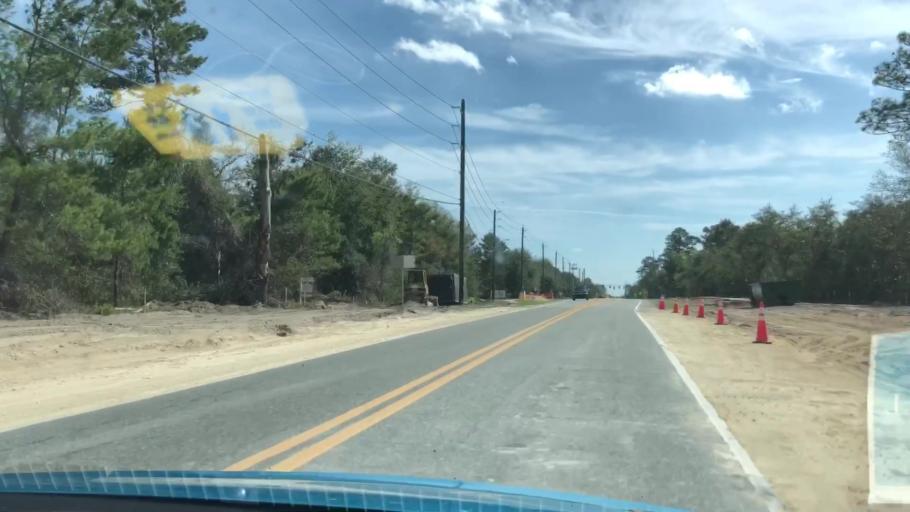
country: US
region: Florida
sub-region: Seminole County
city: Midway
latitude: 28.8575
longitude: -81.1902
